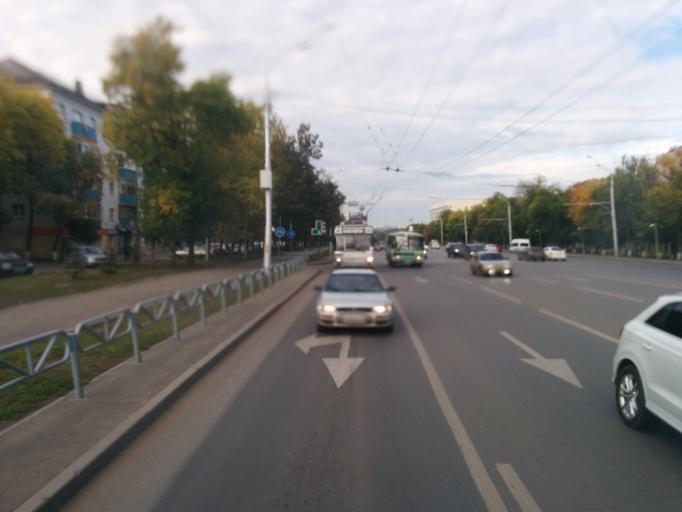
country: RU
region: Bashkortostan
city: Ufa
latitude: 54.7905
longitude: 56.0361
